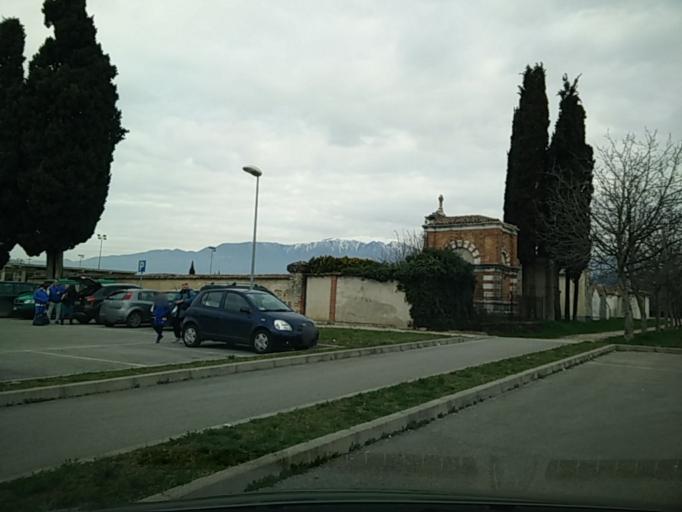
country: IT
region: Veneto
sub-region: Provincia di Treviso
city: Asolo
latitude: 45.7833
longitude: 11.9219
